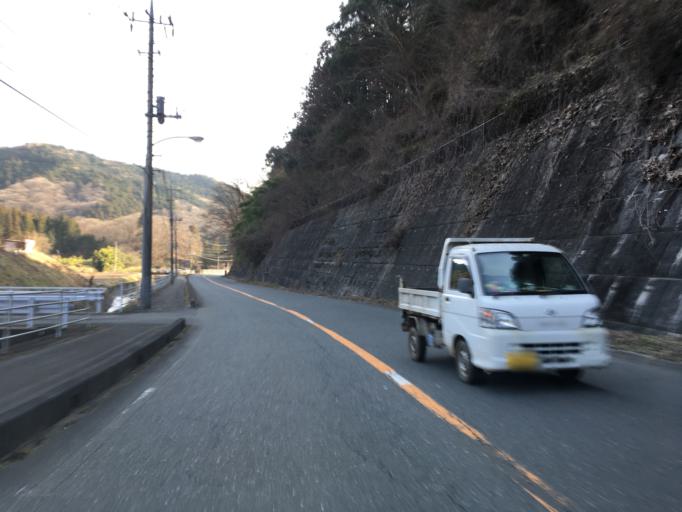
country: JP
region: Ibaraki
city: Daigo
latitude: 36.7248
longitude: 140.5085
